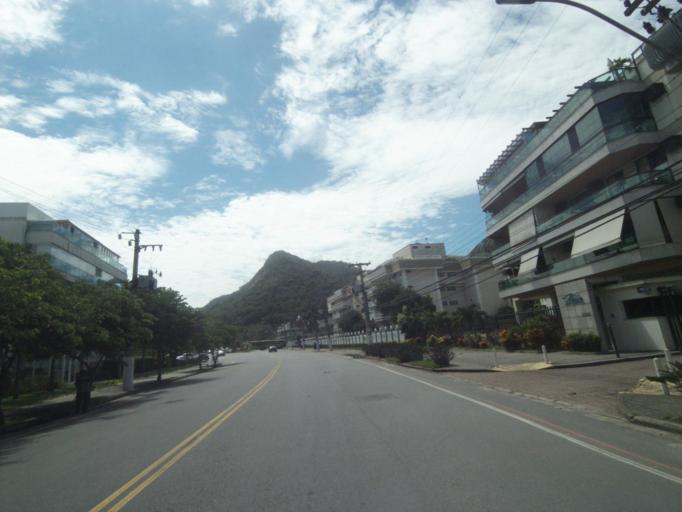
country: BR
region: Rio de Janeiro
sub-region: Niteroi
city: Niteroi
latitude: -22.9645
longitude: -43.0330
